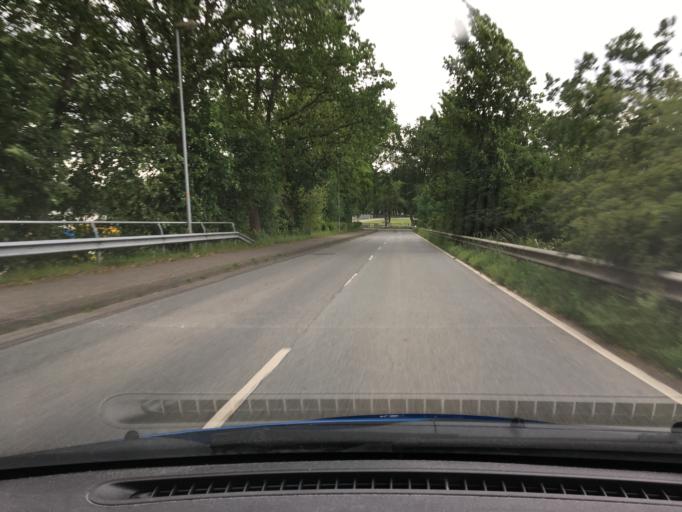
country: DE
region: Lower Saxony
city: Sittensen
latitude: 53.2897
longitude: 9.4997
